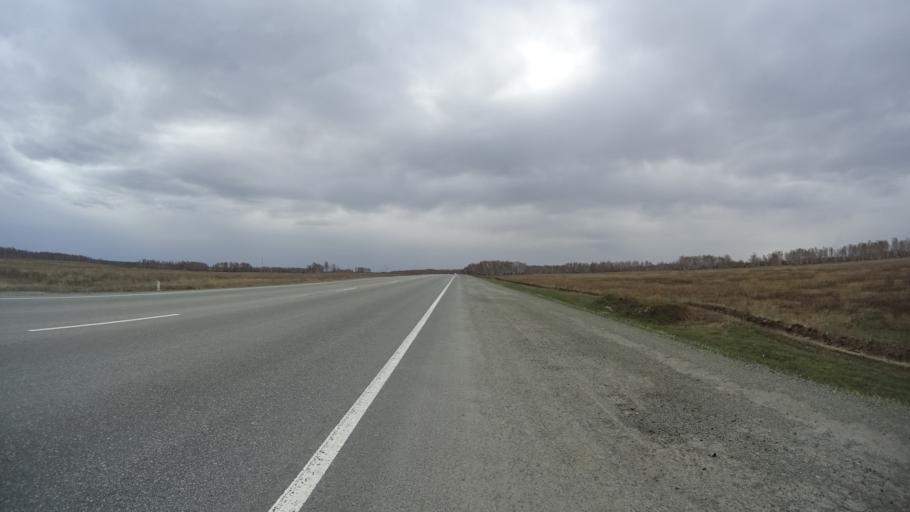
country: RU
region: Chelyabinsk
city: Yemanzhelinsk
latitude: 54.7036
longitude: 61.2548
